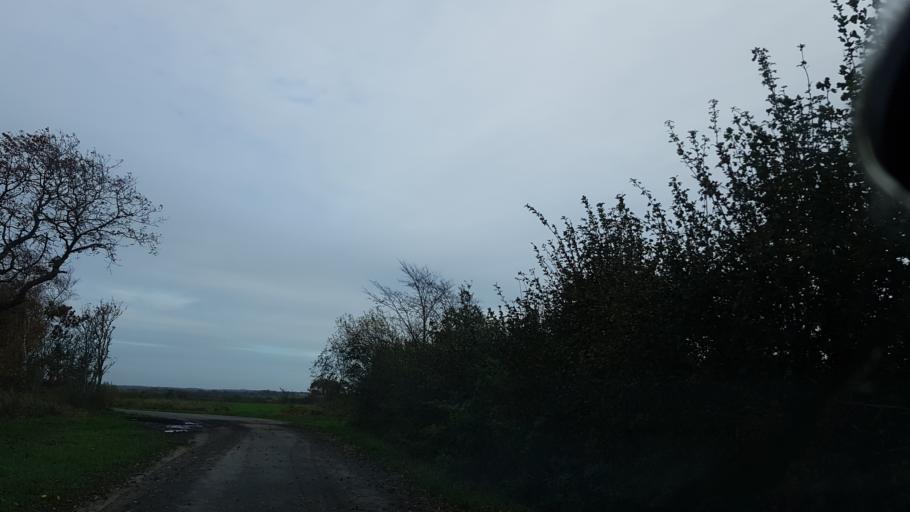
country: DK
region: South Denmark
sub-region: Tonder Kommune
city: Sherrebek
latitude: 55.2243
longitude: 8.8714
